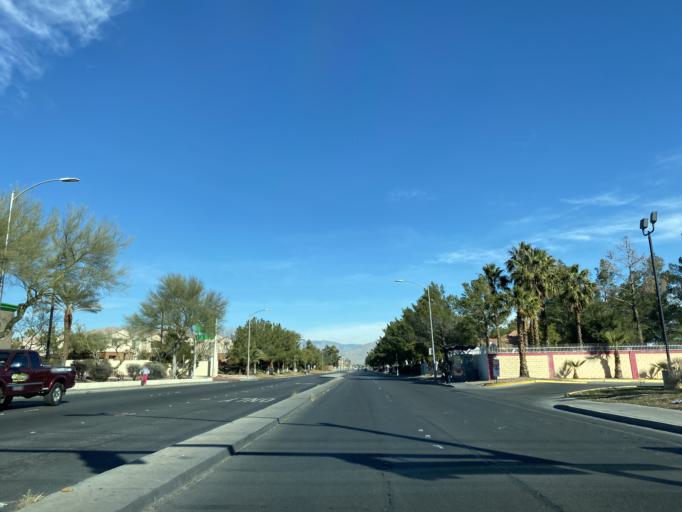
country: US
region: Nevada
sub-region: Clark County
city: Spring Valley
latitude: 36.1887
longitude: -115.2240
